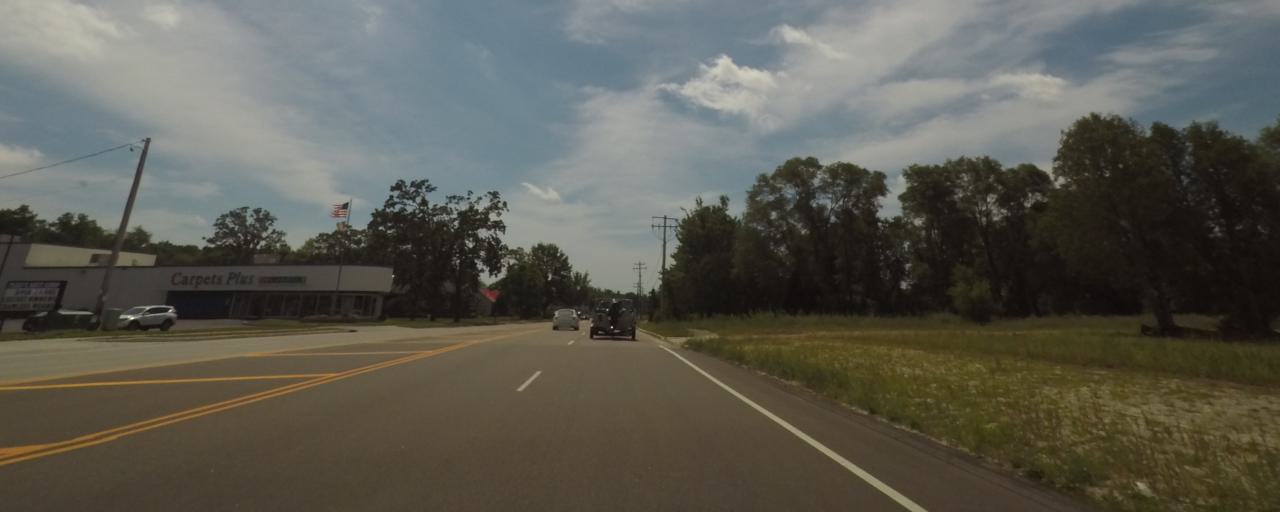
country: US
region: Wisconsin
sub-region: Portage County
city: Whiting
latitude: 44.4799
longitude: -89.5490
